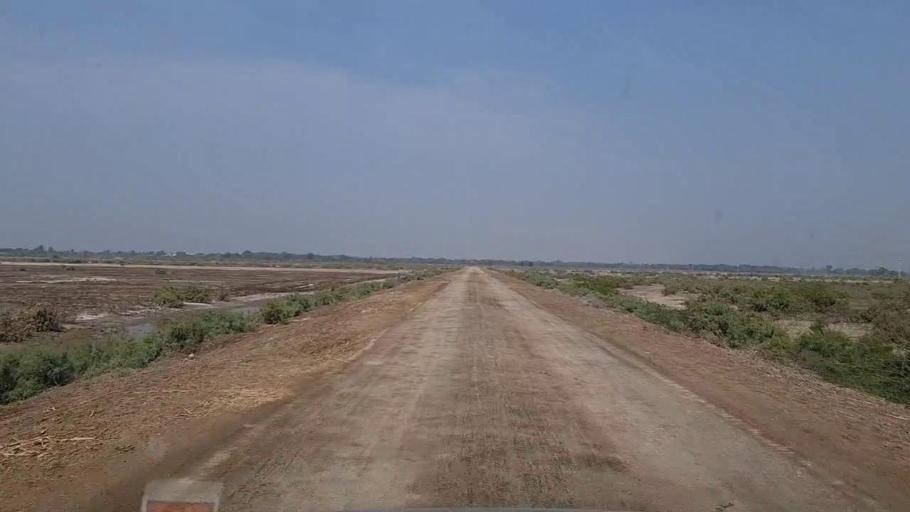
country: PK
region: Sindh
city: Mirwah Gorchani
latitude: 25.3305
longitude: 69.0615
